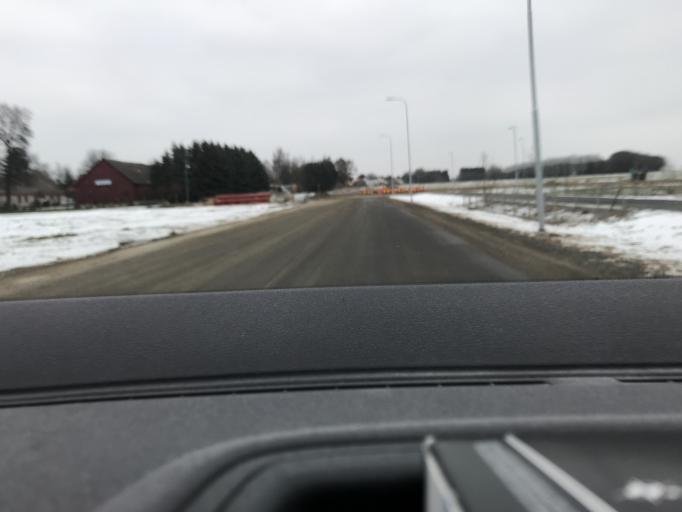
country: SE
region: Skane
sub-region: Ystads Kommun
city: Ystad
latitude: 55.4557
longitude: 13.8529
